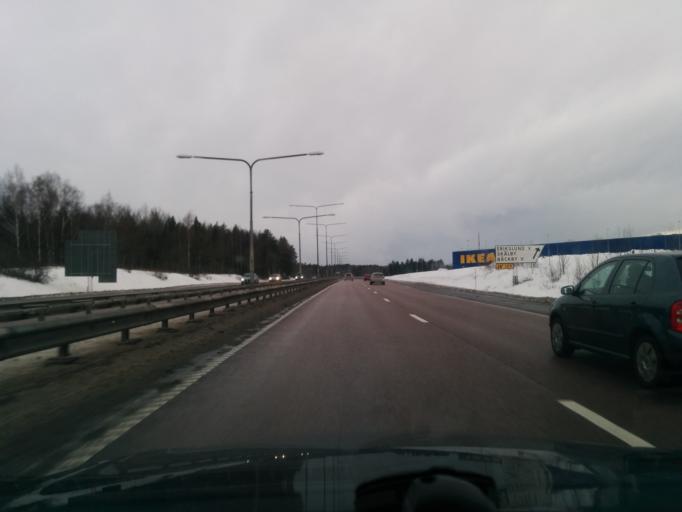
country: SE
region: Vaestmanland
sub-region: Vasteras
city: Vasteras
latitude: 59.6075
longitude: 16.4624
